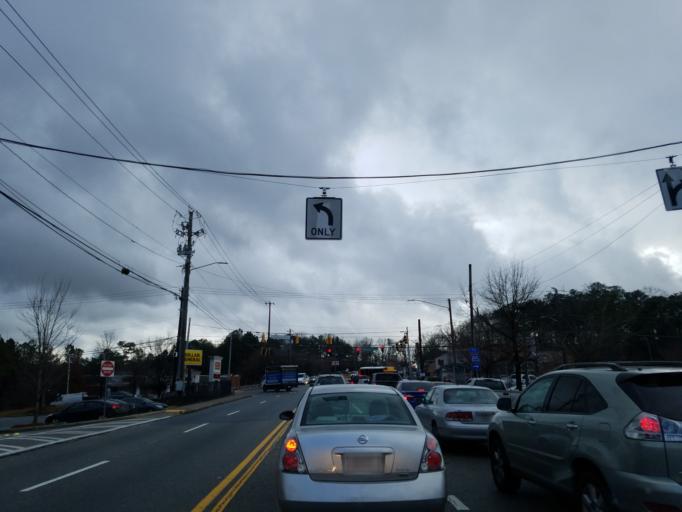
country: US
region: Georgia
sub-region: Fulton County
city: Hapeville
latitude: 33.6820
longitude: -84.4077
